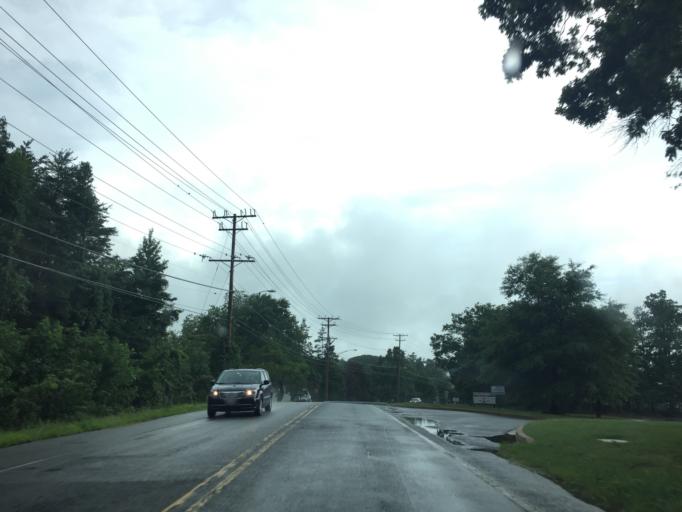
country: US
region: Maryland
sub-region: Harford County
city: Bel Air South
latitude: 39.4703
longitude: -76.2925
